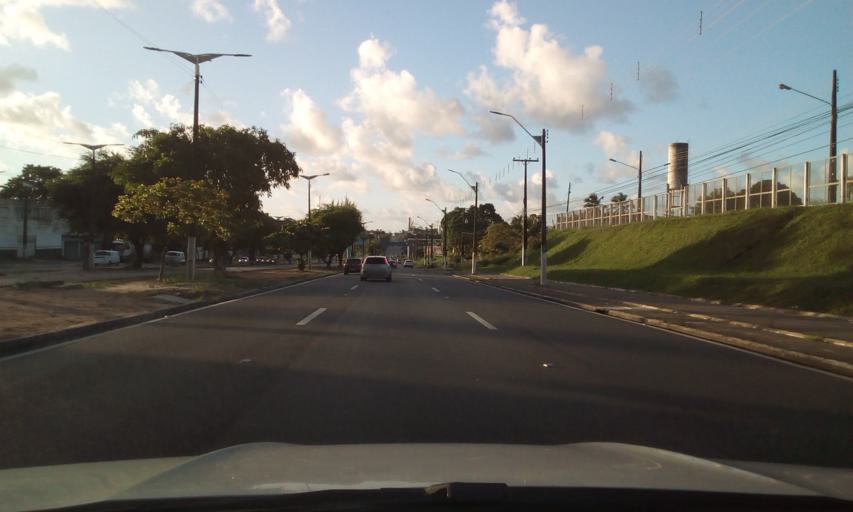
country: BR
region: Pernambuco
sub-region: Abreu E Lima
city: Abreu e Lima
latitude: -7.8898
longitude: -34.9036
